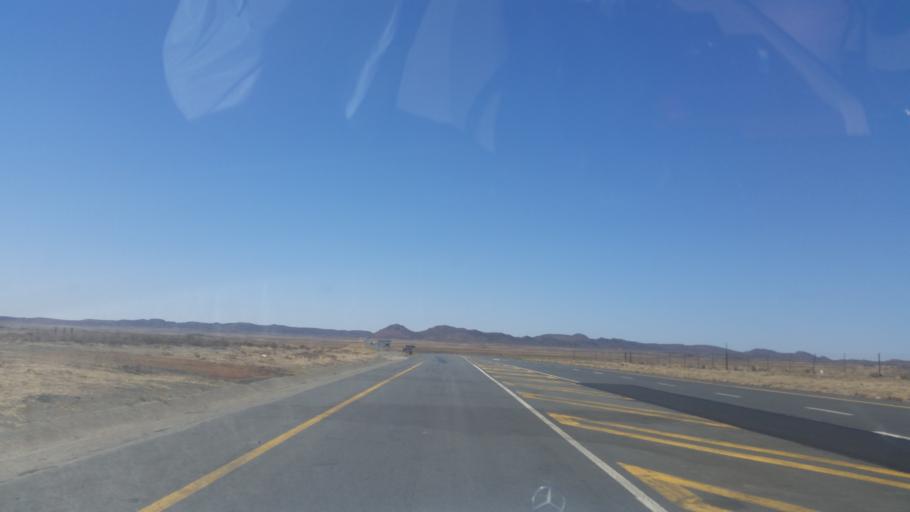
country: ZA
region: Northern Cape
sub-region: Pixley ka Seme District Municipality
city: Colesberg
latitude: -30.6875
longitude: 25.1530
